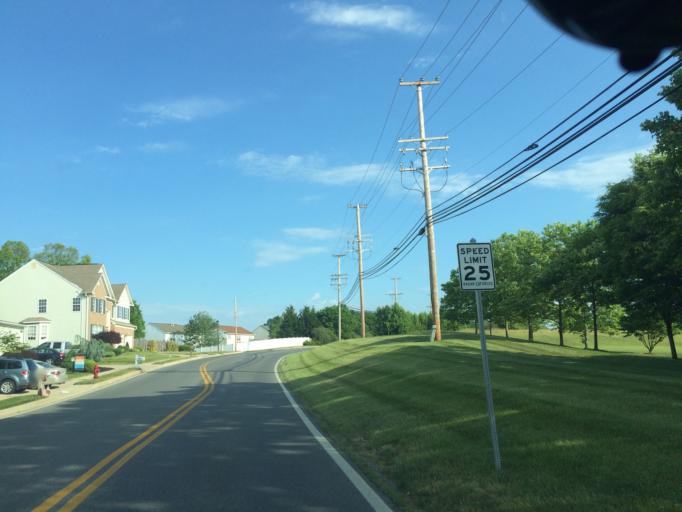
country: US
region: Maryland
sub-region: Carroll County
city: Sykesville
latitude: 39.3776
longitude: -76.9767
